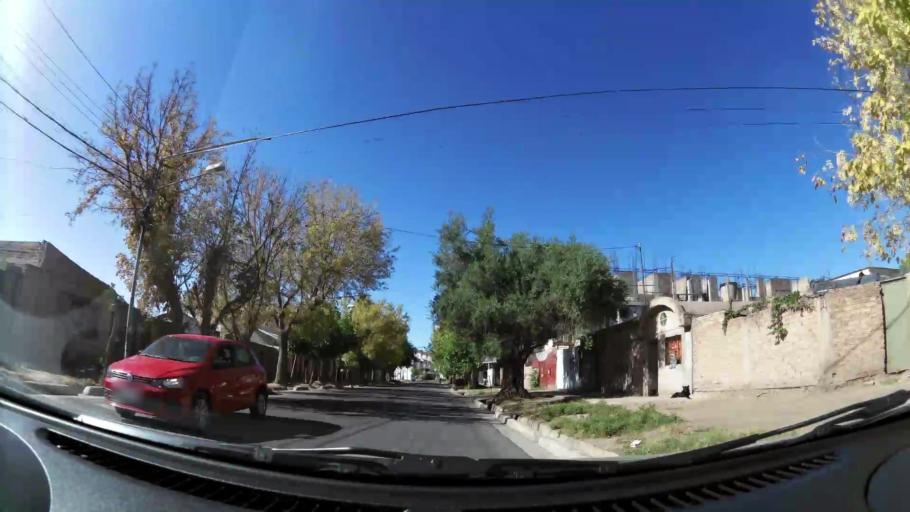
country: AR
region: Mendoza
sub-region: Departamento de Godoy Cruz
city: Godoy Cruz
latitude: -32.9306
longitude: -68.8622
